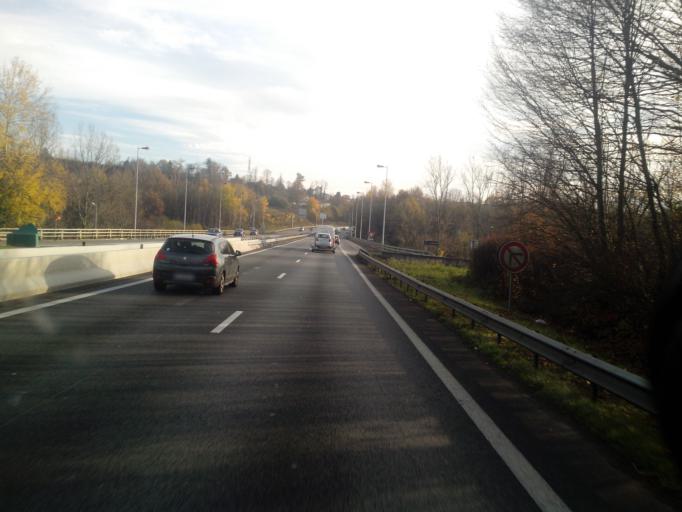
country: FR
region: Limousin
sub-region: Departement de la Haute-Vienne
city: Limoges
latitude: 45.8383
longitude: 1.2821
